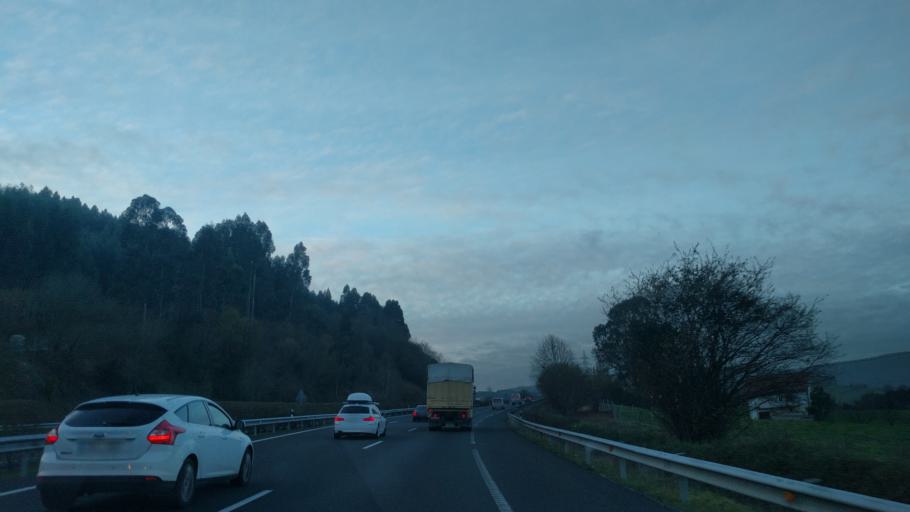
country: ES
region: Cantabria
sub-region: Provincia de Cantabria
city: Barcena de Cicero
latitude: 43.4091
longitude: -3.5141
